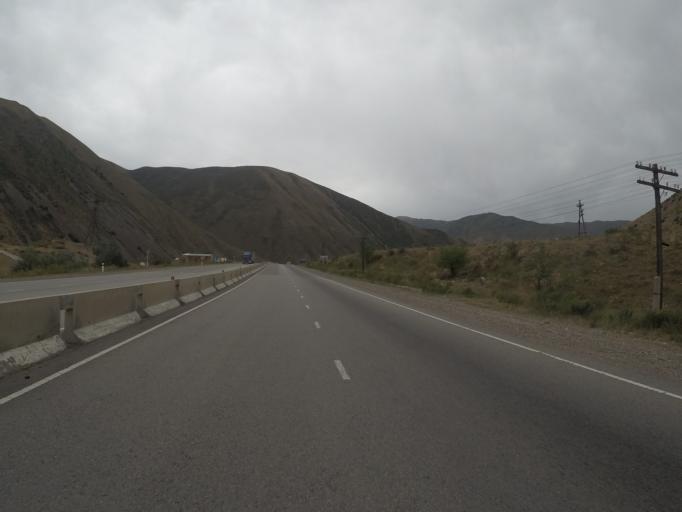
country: KG
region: Chuy
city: Bystrovka
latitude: 42.6810
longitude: 75.8916
